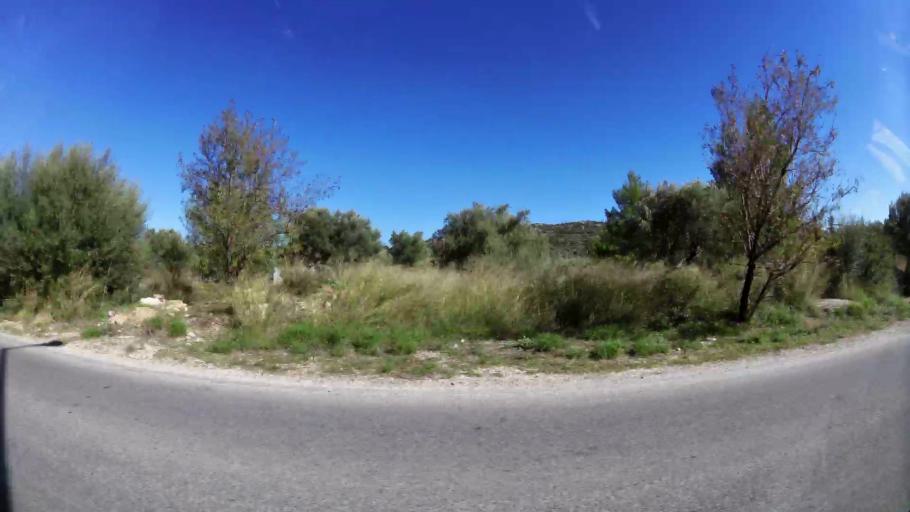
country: GR
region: Attica
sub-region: Nomarchia Anatolikis Attikis
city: Paiania
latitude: 37.9654
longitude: 23.8641
